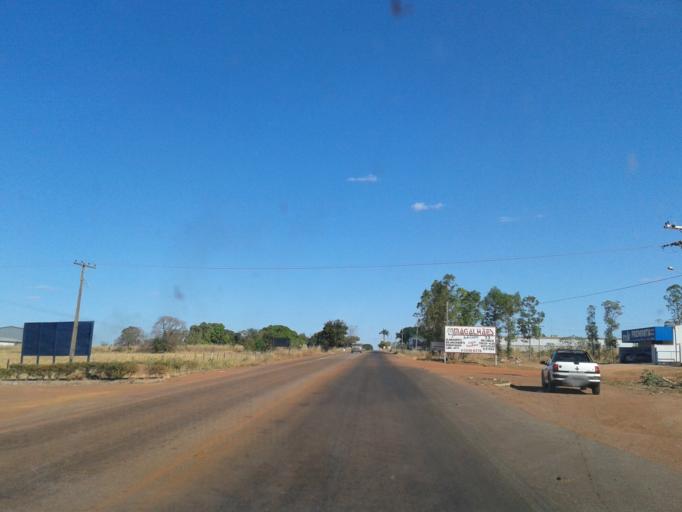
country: BR
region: Goias
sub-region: Mozarlandia
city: Mozarlandia
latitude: -14.7590
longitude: -50.5395
